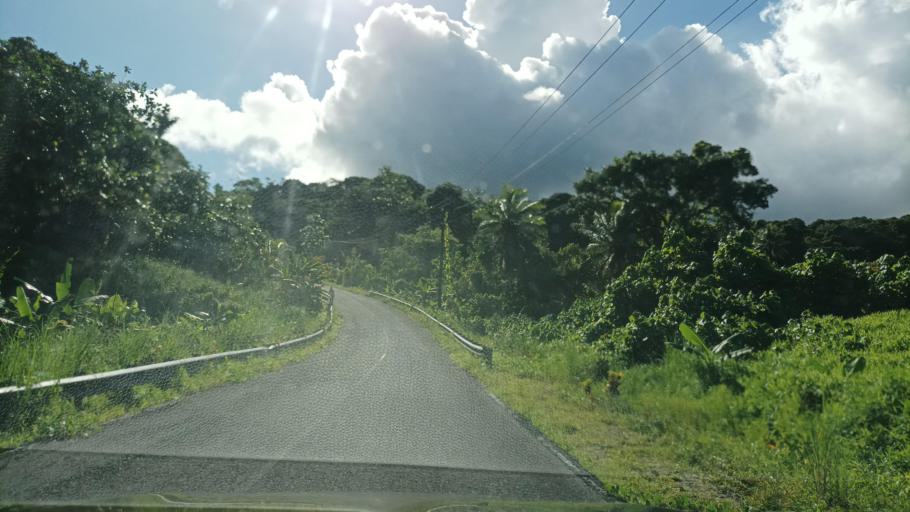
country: FM
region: Pohnpei
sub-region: Madolenihm Municipality
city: Madolenihm Municipality Government
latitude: 6.8123
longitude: 158.2920
